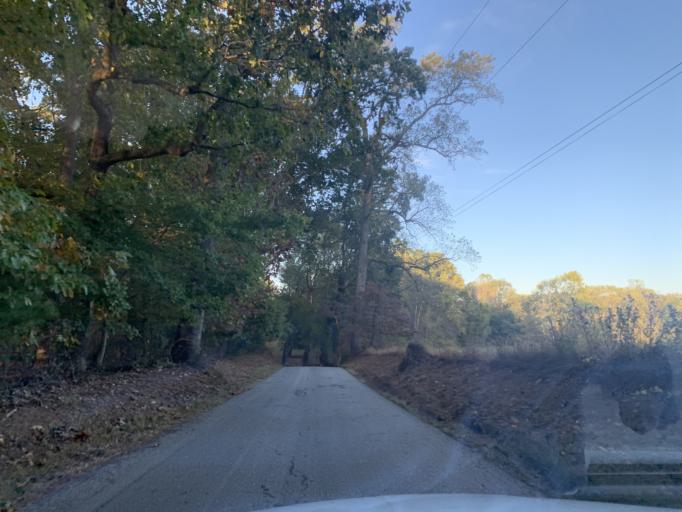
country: US
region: Maryland
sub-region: Harford County
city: Fallston
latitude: 39.5018
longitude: -76.4344
